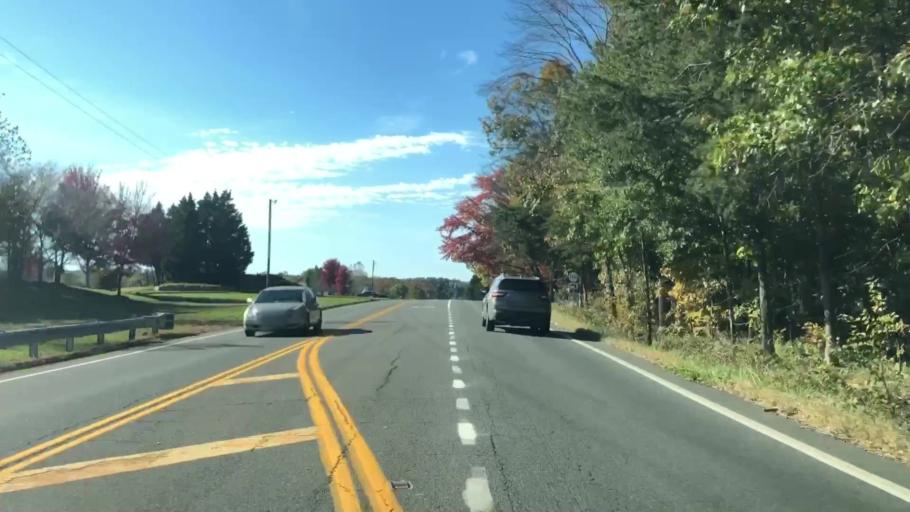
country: US
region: Virginia
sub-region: Fauquier County
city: New Baltimore
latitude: 38.7540
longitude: -77.6683
